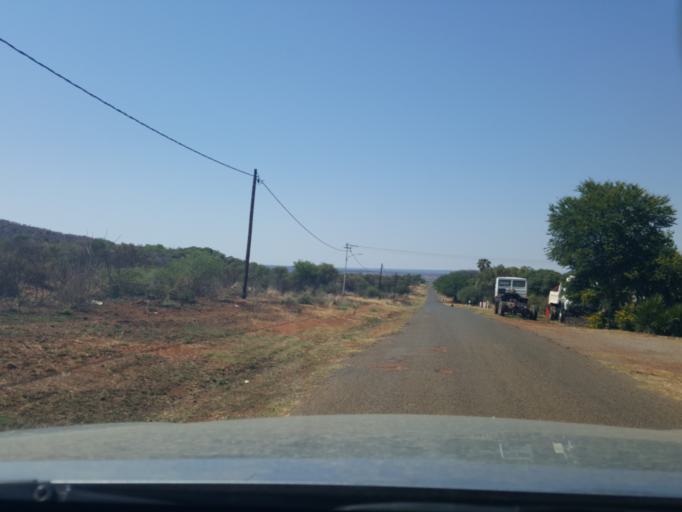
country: ZA
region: North-West
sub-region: Ngaka Modiri Molema District Municipality
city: Zeerust
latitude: -25.5260
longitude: 26.0801
